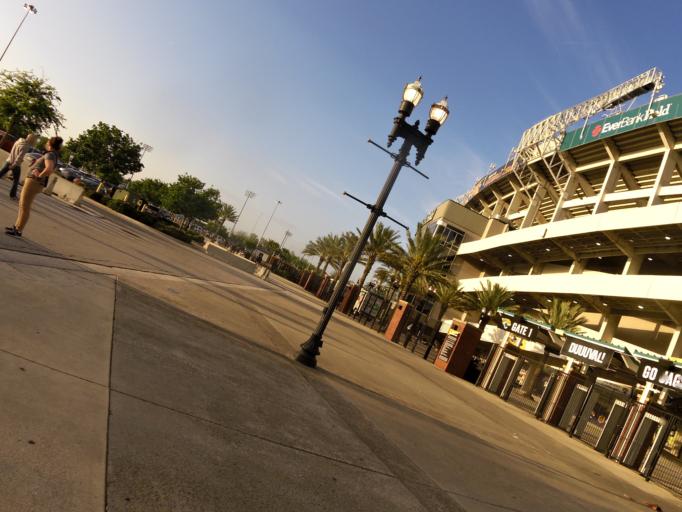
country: US
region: Florida
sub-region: Duval County
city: Jacksonville
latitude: 30.3233
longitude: -81.6391
